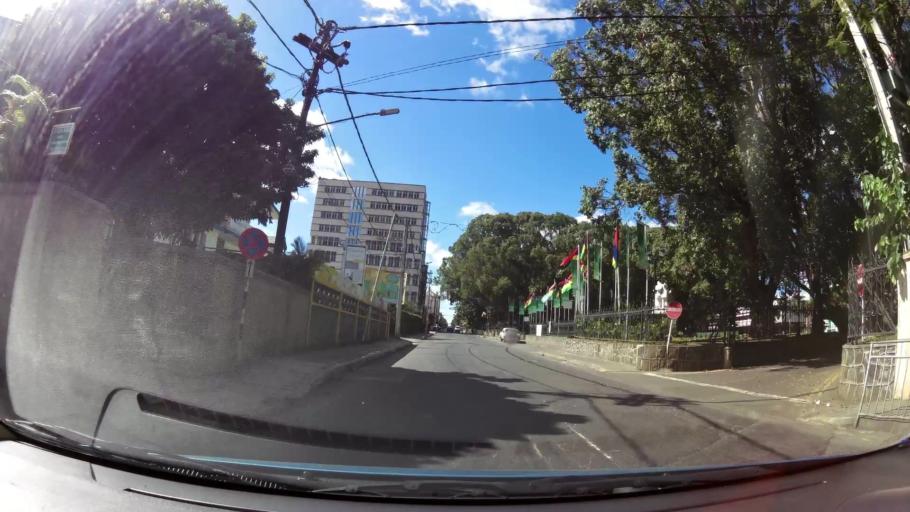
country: MU
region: Plaines Wilhems
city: Vacoas
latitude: -20.2999
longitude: 57.4907
